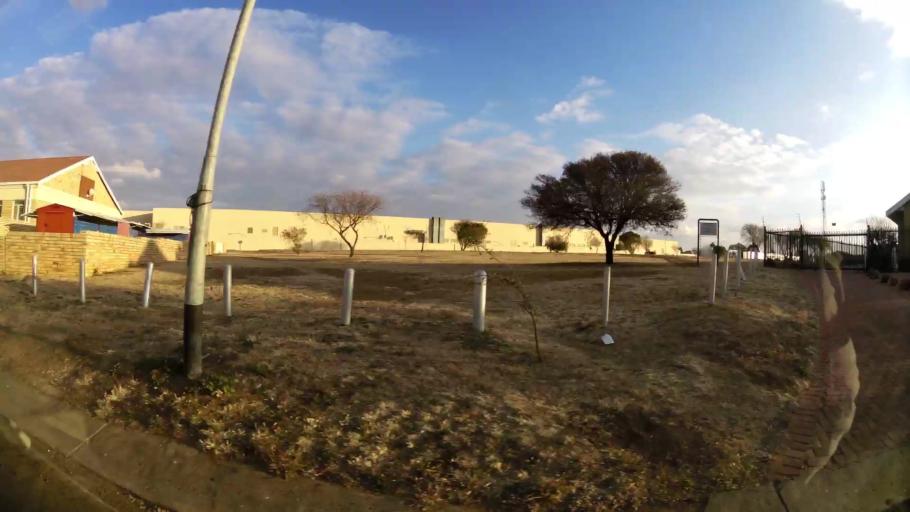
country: ZA
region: Orange Free State
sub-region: Mangaung Metropolitan Municipality
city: Bloemfontein
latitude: -29.1431
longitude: 26.1797
